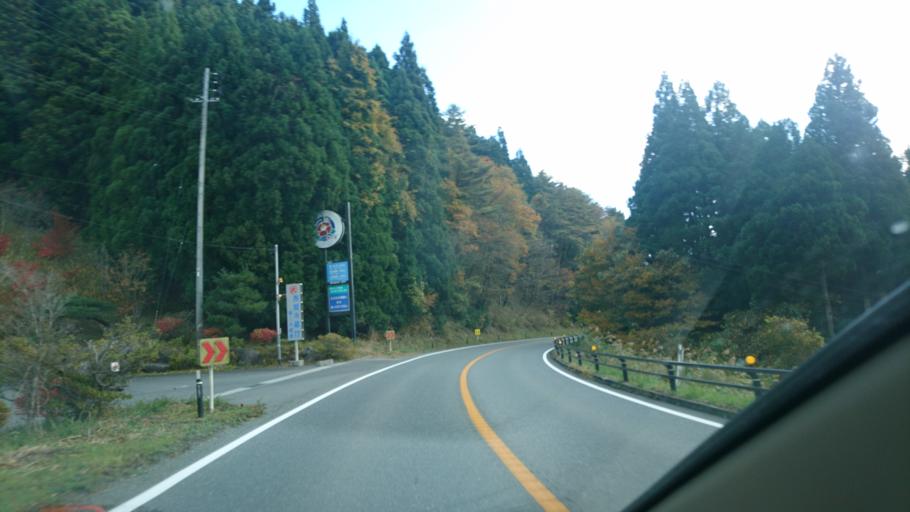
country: JP
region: Iwate
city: Ofunato
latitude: 39.0286
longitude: 141.6966
